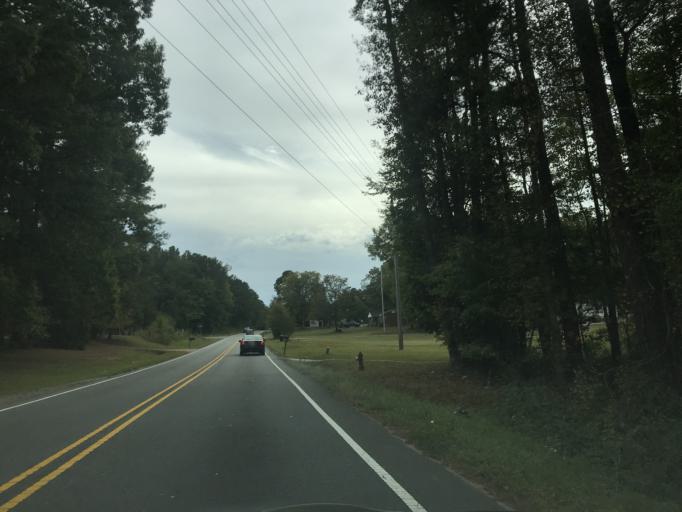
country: US
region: North Carolina
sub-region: Wake County
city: Rolesville
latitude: 35.9077
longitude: -78.5050
